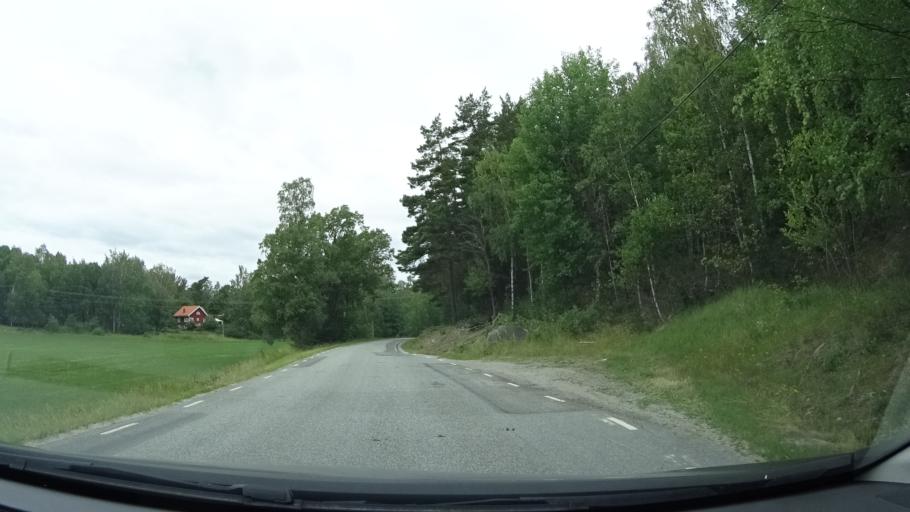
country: SE
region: Stockholm
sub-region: Varmdo Kommun
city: Mortnas
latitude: 59.3666
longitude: 18.4669
